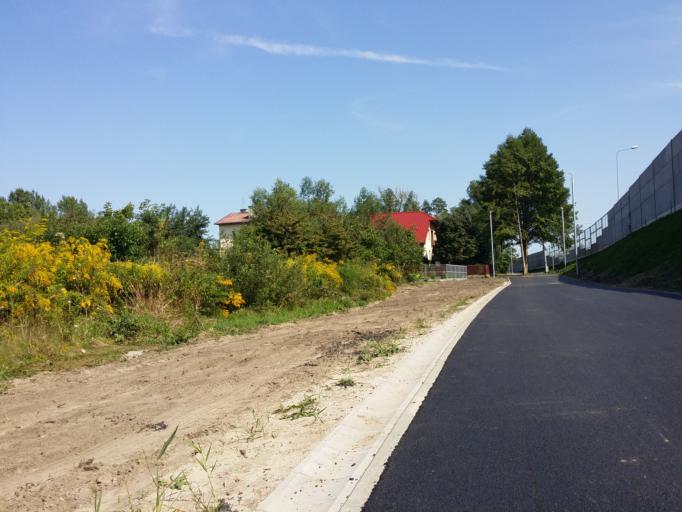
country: PL
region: Masovian Voivodeship
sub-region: Radom
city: Radom
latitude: 51.3713
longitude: 21.1582
